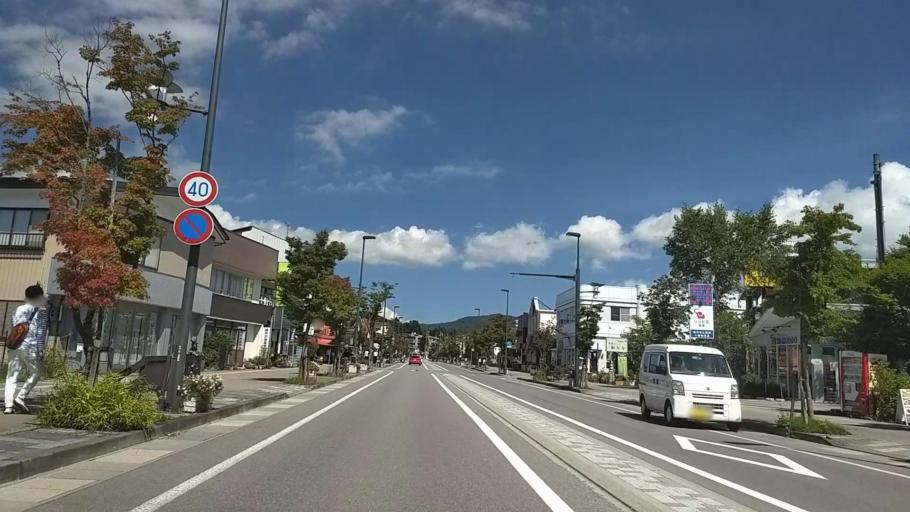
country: JP
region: Nagano
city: Saku
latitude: 36.3455
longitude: 138.6352
